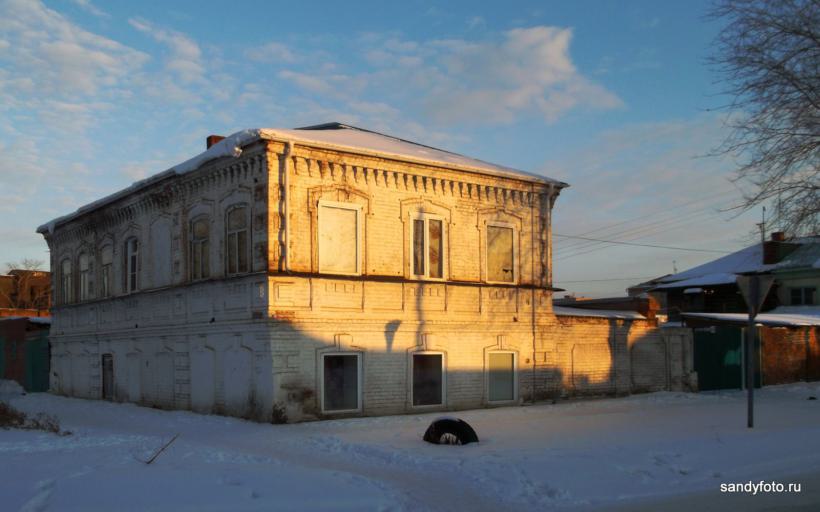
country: RU
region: Chelyabinsk
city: Troitsk
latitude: 54.0886
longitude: 61.5505
